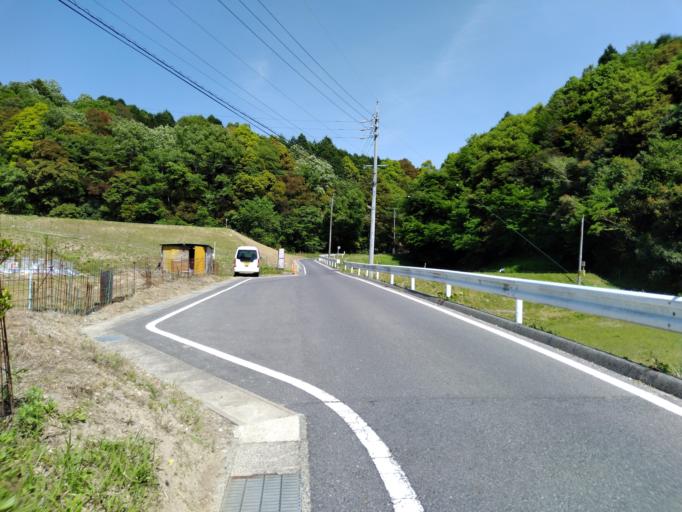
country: JP
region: Gifu
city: Toki
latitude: 35.2464
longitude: 137.2331
